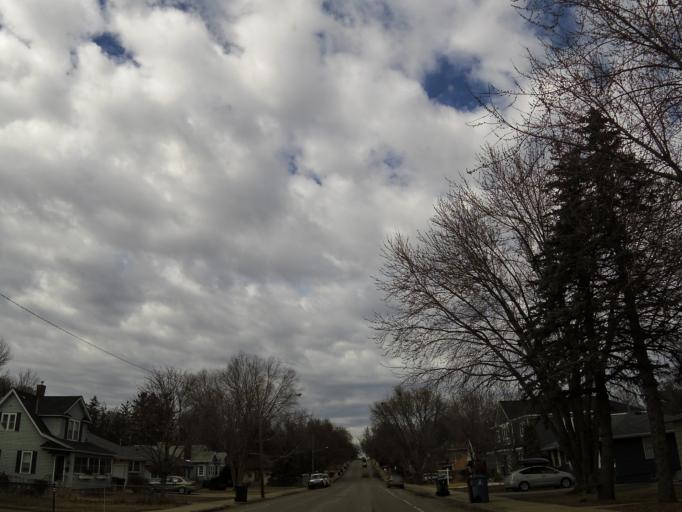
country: US
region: Minnesota
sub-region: Hennepin County
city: Edina
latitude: 44.9168
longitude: -93.3189
